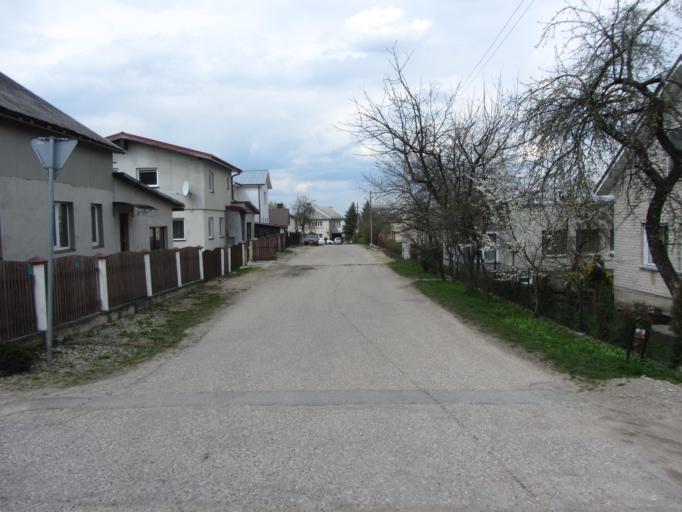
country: LT
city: Lentvaris
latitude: 54.6539
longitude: 25.0499
